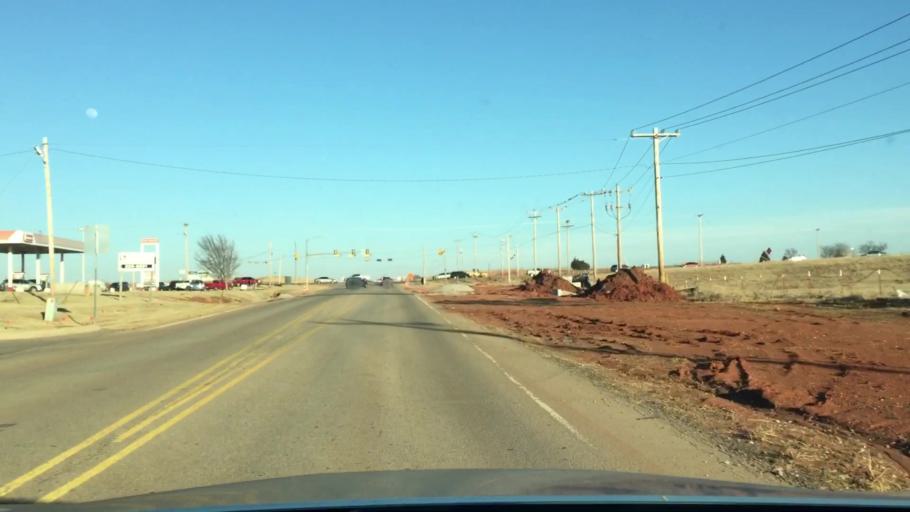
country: US
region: Oklahoma
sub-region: Oklahoma County
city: The Village
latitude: 35.6531
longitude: -97.5872
